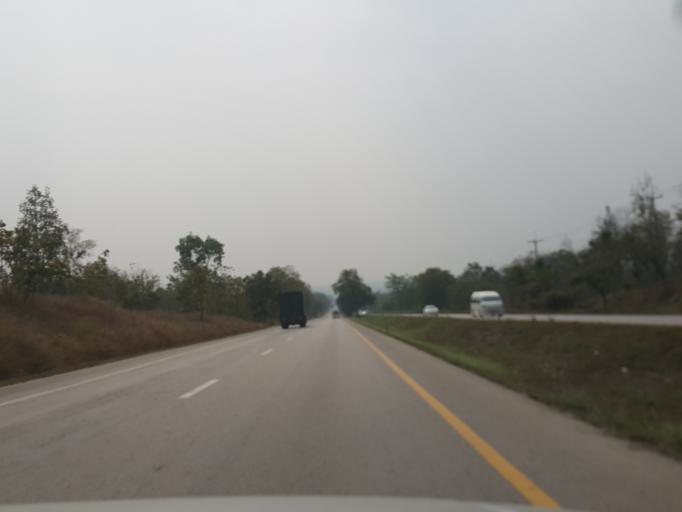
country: TH
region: Lampang
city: Ko Kha
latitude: 18.0902
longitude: 99.3965
